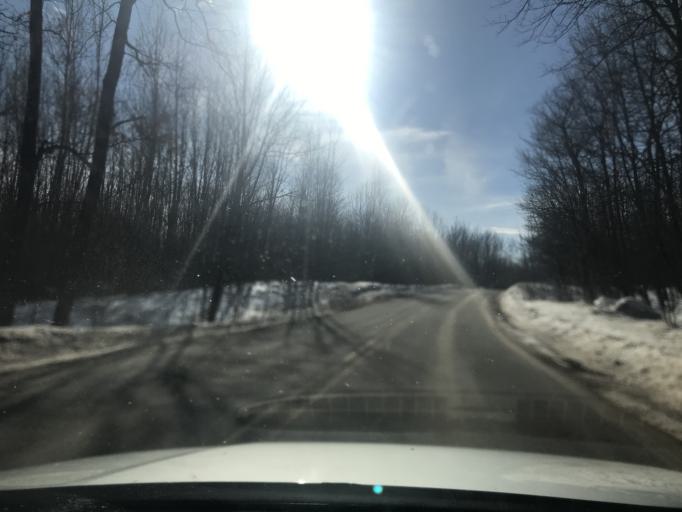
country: US
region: Michigan
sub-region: Dickinson County
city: Kingsford
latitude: 45.4002
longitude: -88.3412
